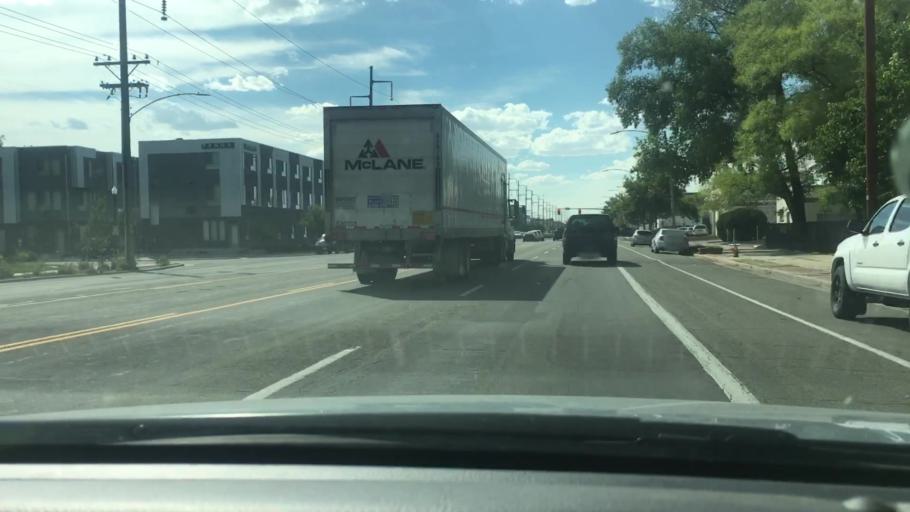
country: US
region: Utah
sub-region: Salt Lake County
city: Salt Lake City
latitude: 40.7520
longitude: -111.8976
